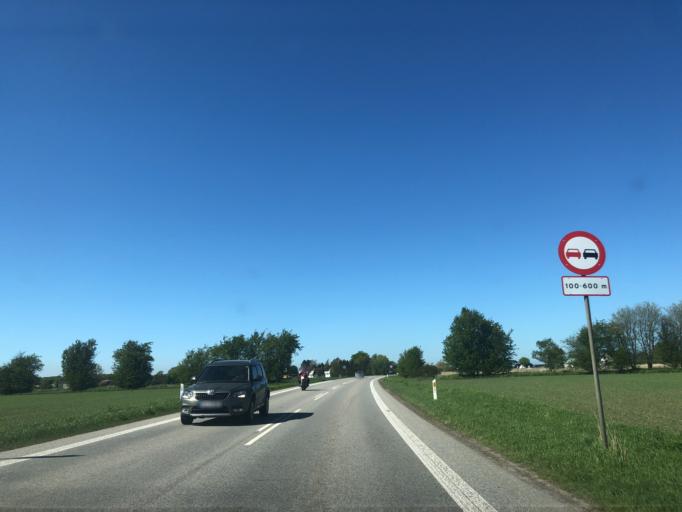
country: DK
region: Zealand
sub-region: Stevns Kommune
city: Store Heddinge
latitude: 55.3073
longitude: 12.3706
